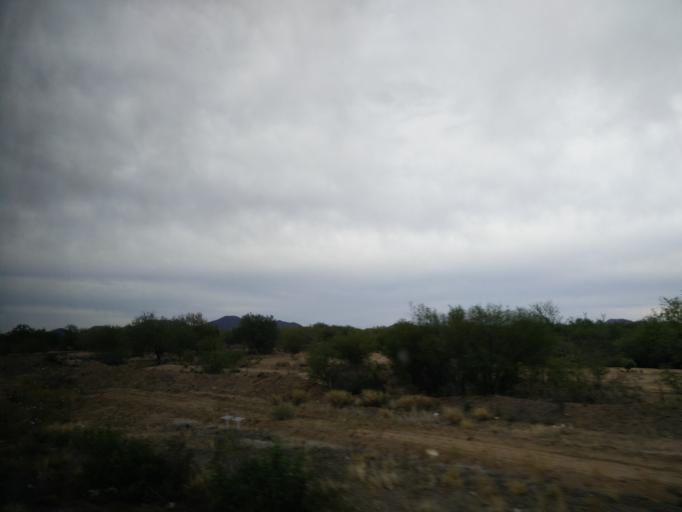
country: MX
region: Sonora
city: Hermosillo
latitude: 28.7416
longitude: -110.9753
